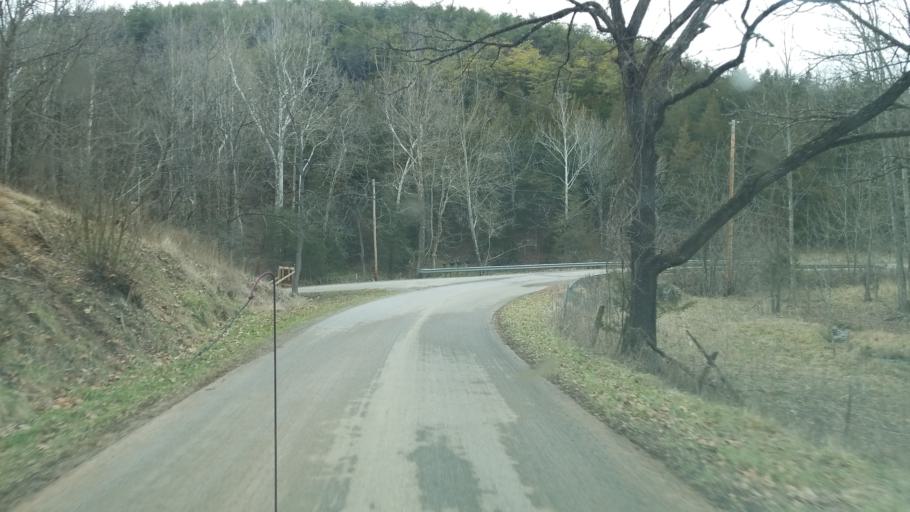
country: US
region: Virginia
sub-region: Giles County
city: Pearisburg
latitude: 37.2303
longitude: -80.7057
